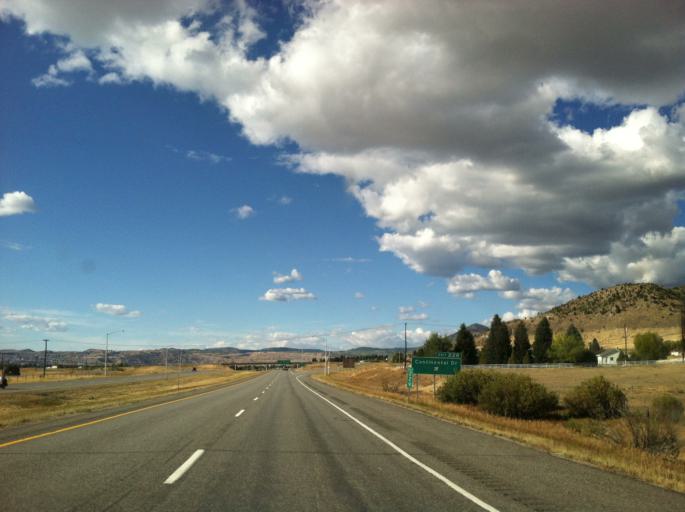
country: US
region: Montana
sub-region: Silver Bow County
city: Butte
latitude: 45.9566
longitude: -112.4696
